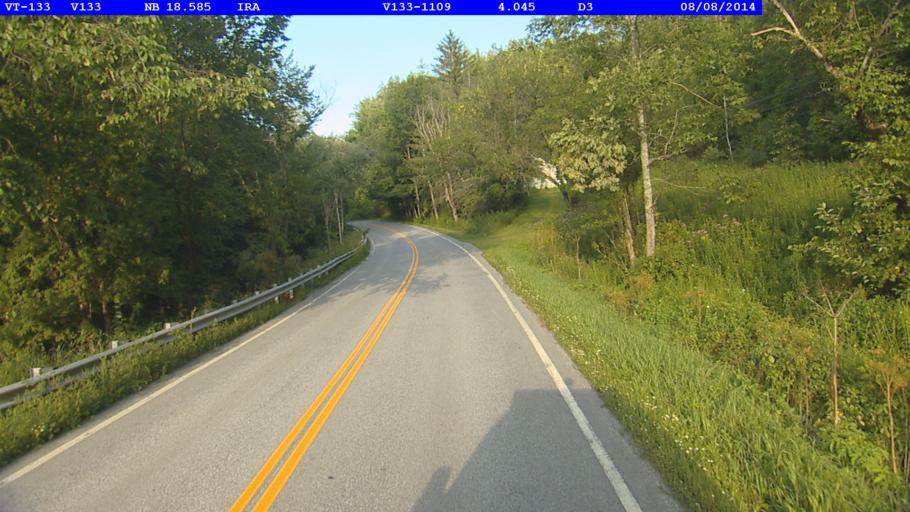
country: US
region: Vermont
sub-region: Rutland County
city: West Rutland
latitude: 43.5440
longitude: -73.0481
